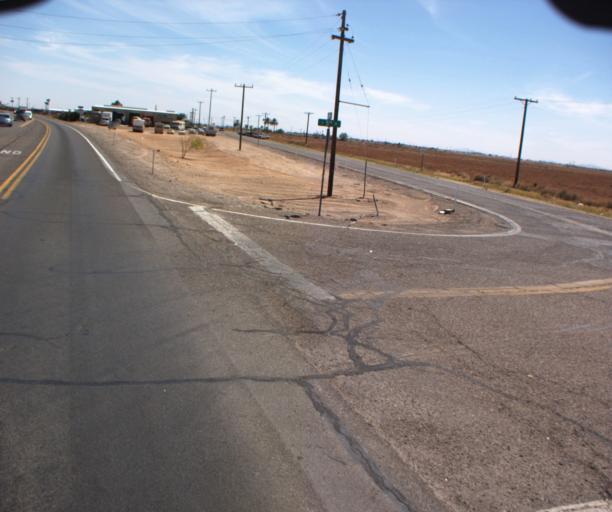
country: US
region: Arizona
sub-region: Pinal County
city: Coolidge
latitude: 32.9581
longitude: -111.5240
